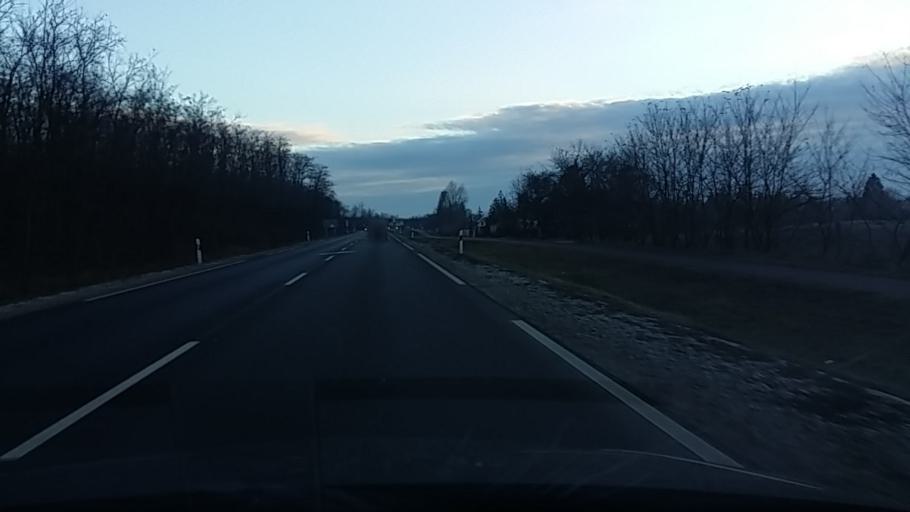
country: HU
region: Hajdu-Bihar
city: Hajduhadhaz
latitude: 47.6267
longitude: 21.6597
